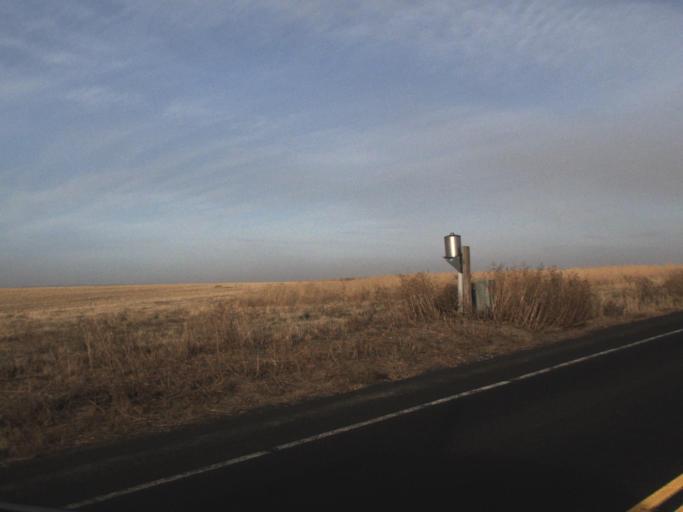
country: US
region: Washington
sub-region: Adams County
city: Ritzville
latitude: 47.1308
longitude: -118.6786
